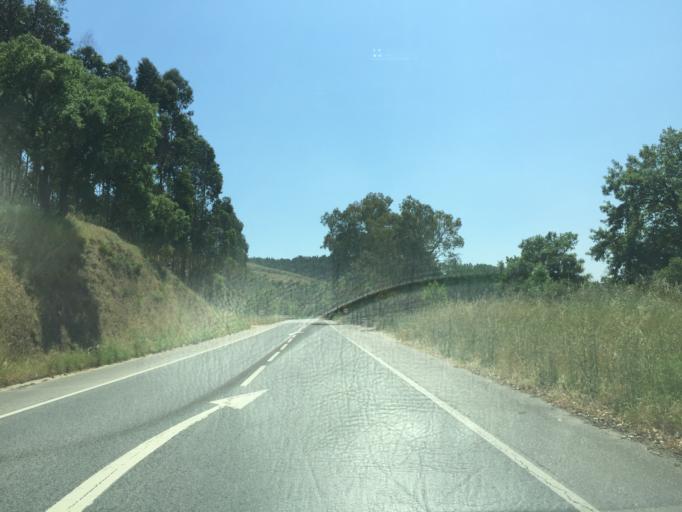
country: PT
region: Santarem
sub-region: Constancia
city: Constancia
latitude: 39.4630
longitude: -8.3433
